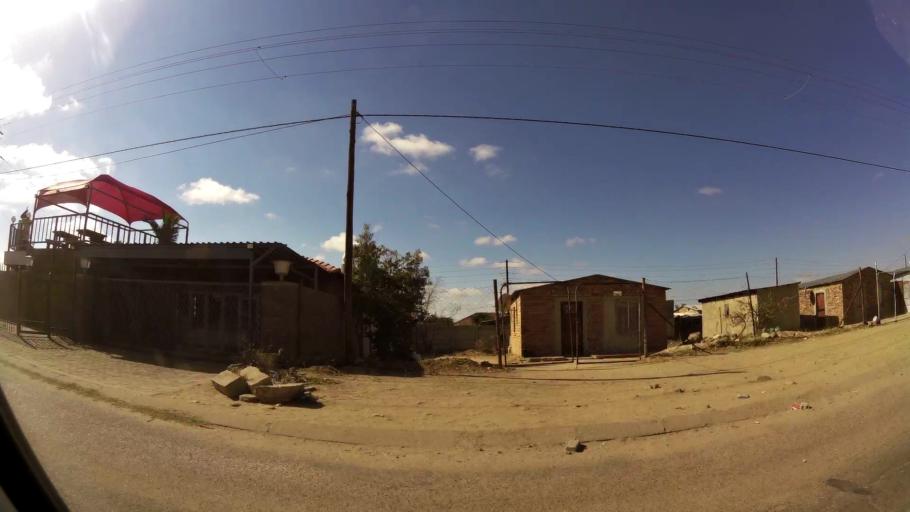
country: ZA
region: Limpopo
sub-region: Capricorn District Municipality
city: Polokwane
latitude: -23.8557
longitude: 29.3969
